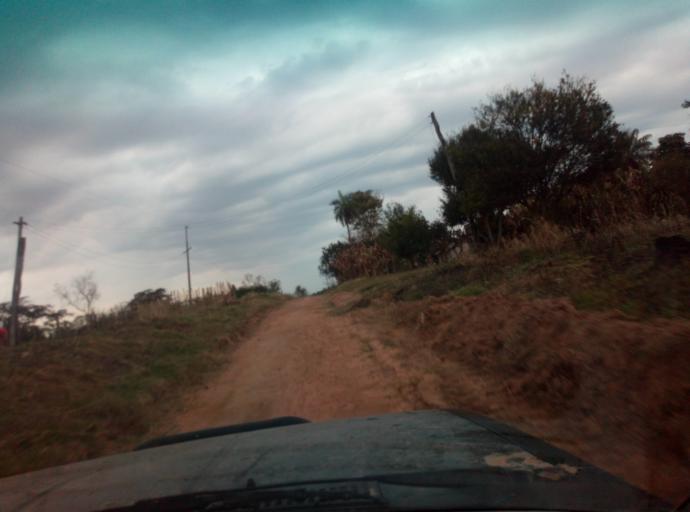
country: PY
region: Caaguazu
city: Doctor Cecilio Baez
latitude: -25.1426
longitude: -56.2241
